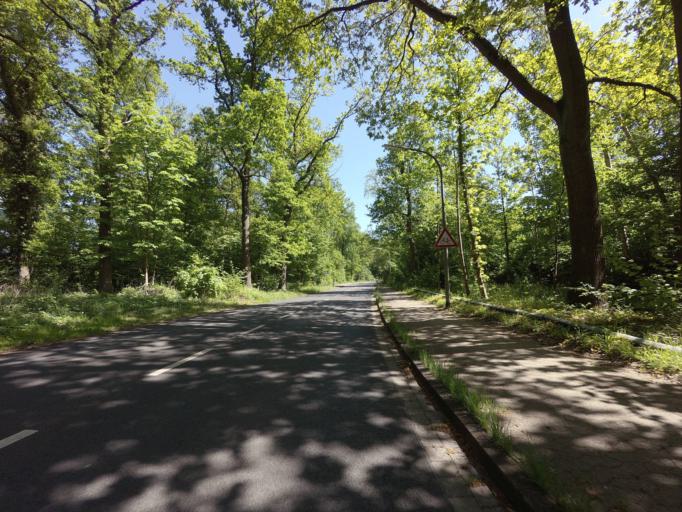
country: DE
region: Lower Saxony
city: Braunschweig
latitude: 52.3083
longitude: 10.5788
